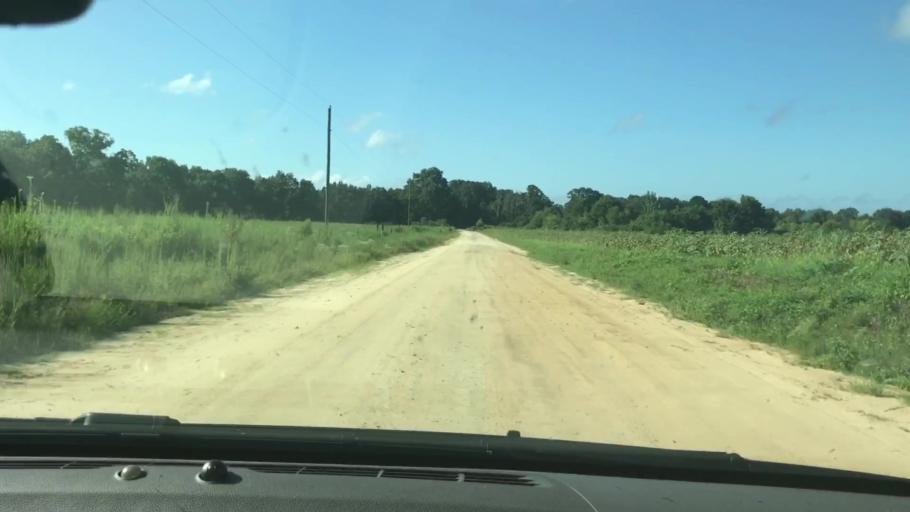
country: US
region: Georgia
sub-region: Clay County
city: Fort Gaines
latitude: 31.7195
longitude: -85.0668
